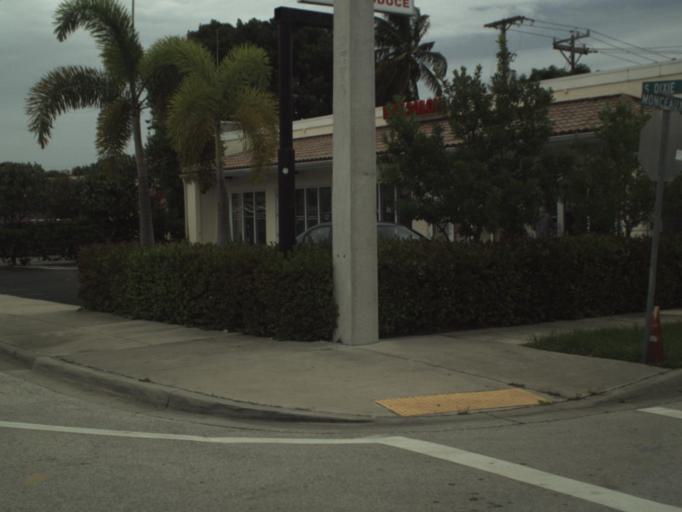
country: US
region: Florida
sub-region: Palm Beach County
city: Palm Beach
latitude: 26.6876
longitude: -80.0544
